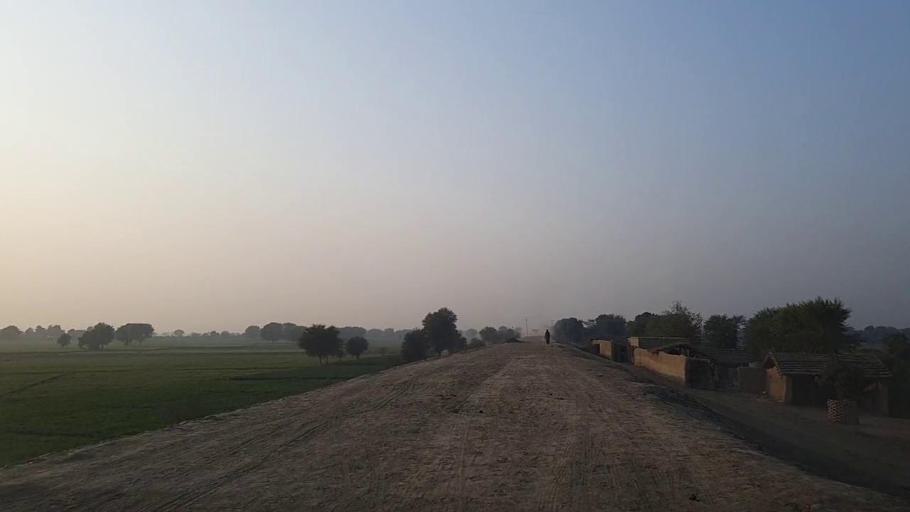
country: PK
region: Sindh
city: Sann
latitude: 26.1726
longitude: 68.1031
